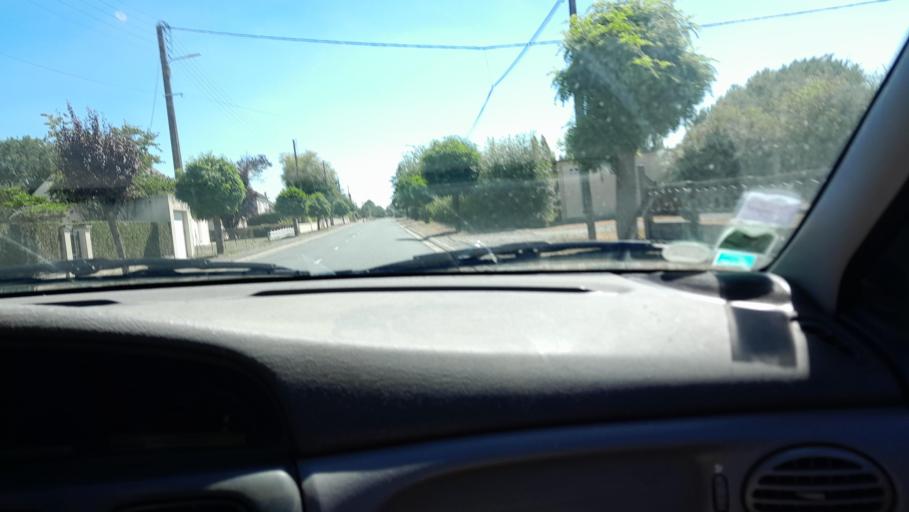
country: FR
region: Pays de la Loire
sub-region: Departement de la Loire-Atlantique
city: Saint-Mars-la-Jaille
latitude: 47.6204
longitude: -1.1980
